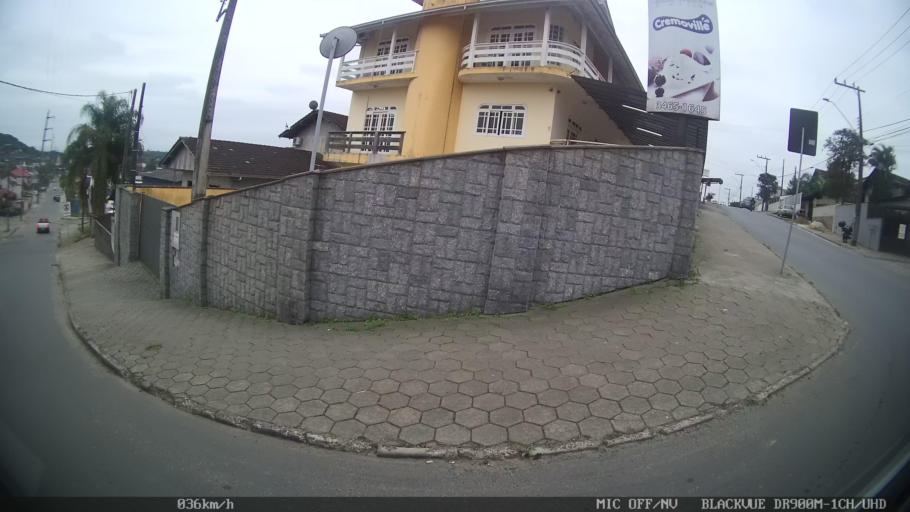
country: BR
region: Santa Catarina
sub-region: Joinville
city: Joinville
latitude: -26.3678
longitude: -48.8244
